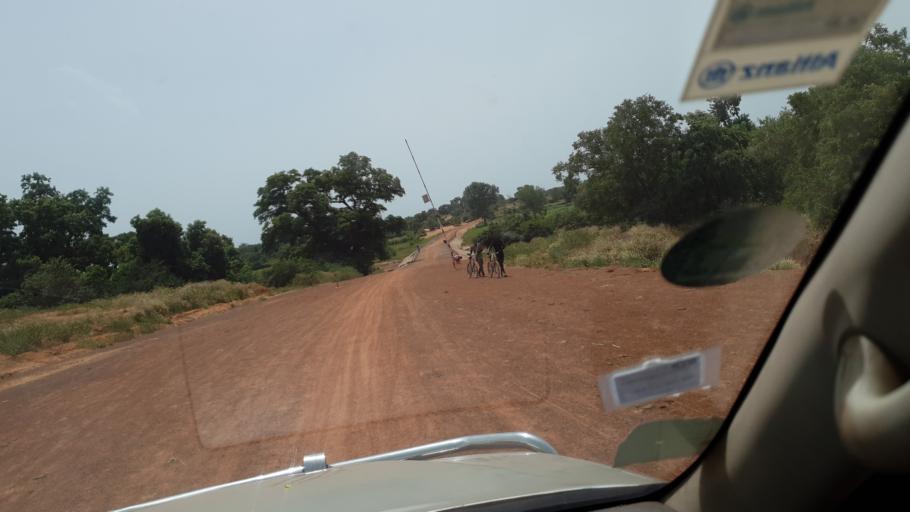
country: ML
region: Koulikoro
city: Kolokani
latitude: 13.4248
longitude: -8.2405
